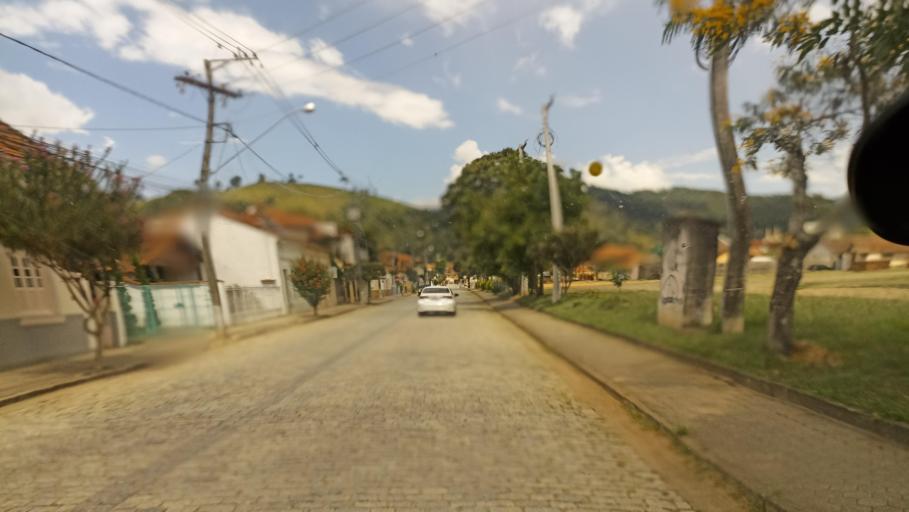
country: BR
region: Minas Gerais
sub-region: Passa Quatro
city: Passa Quatro
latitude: -22.3896
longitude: -44.9651
